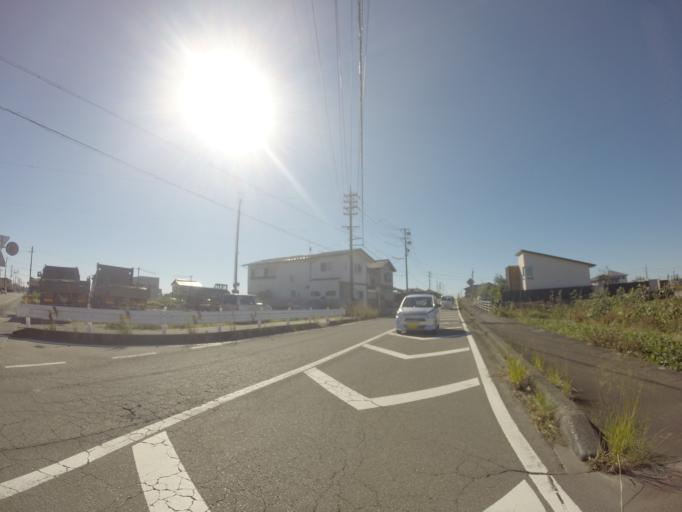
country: JP
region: Shizuoka
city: Fujieda
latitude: 34.8400
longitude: 138.2400
